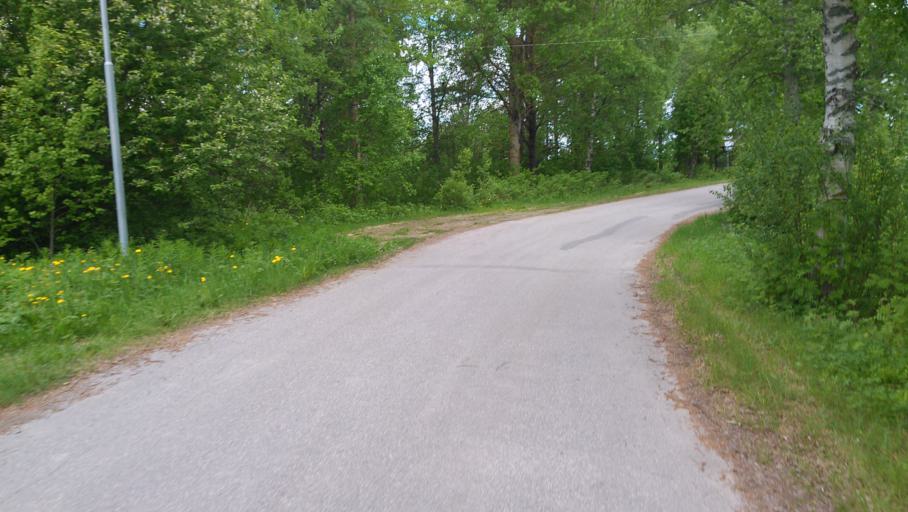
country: SE
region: Vaesterbotten
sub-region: Umea Kommun
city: Roback
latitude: 63.8589
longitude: 20.0891
